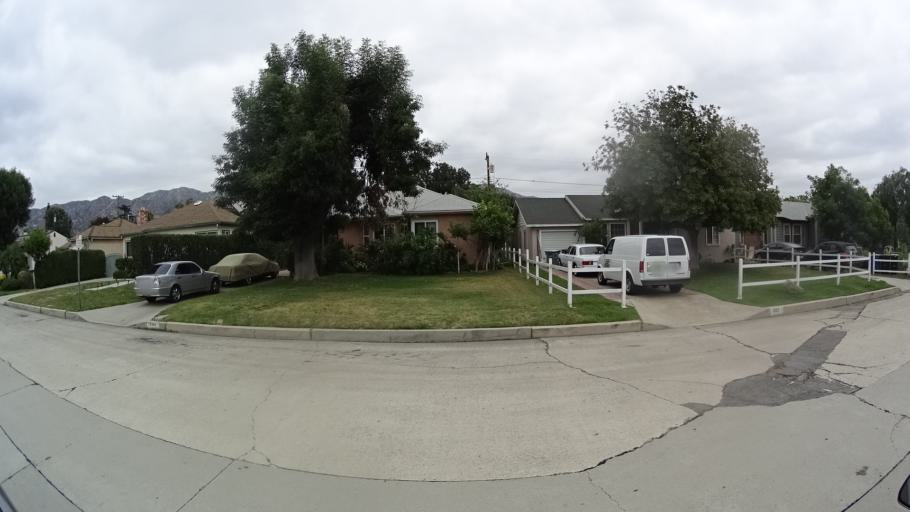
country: US
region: California
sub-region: Los Angeles County
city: Burbank
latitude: 34.1887
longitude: -118.3219
